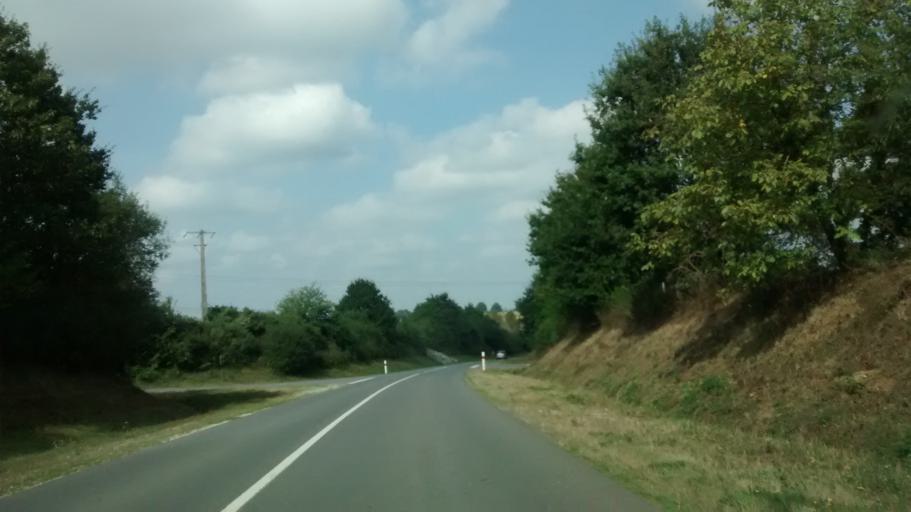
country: FR
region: Brittany
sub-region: Departement d'Ille-et-Vilaine
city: Livre-sur-Changeon
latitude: 48.2254
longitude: -1.3516
